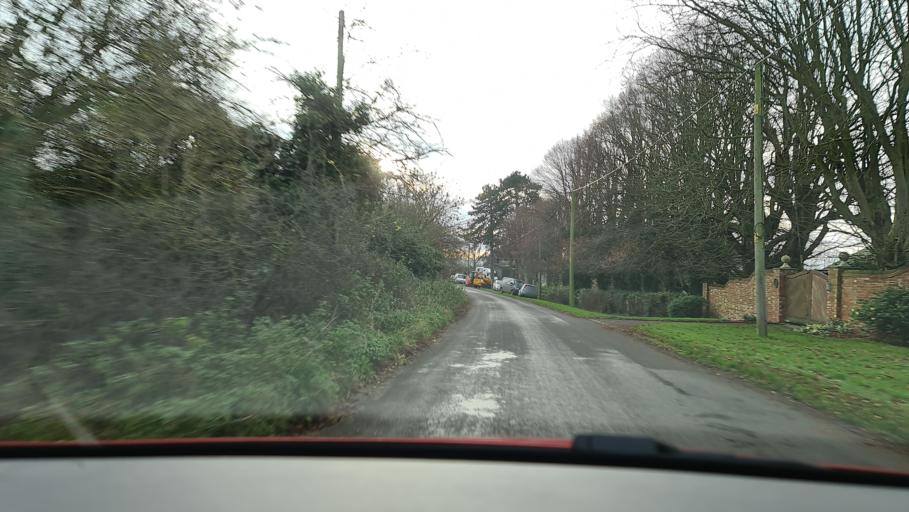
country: GB
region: England
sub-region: Buckinghamshire
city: Long Crendon
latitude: 51.7921
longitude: -0.9657
